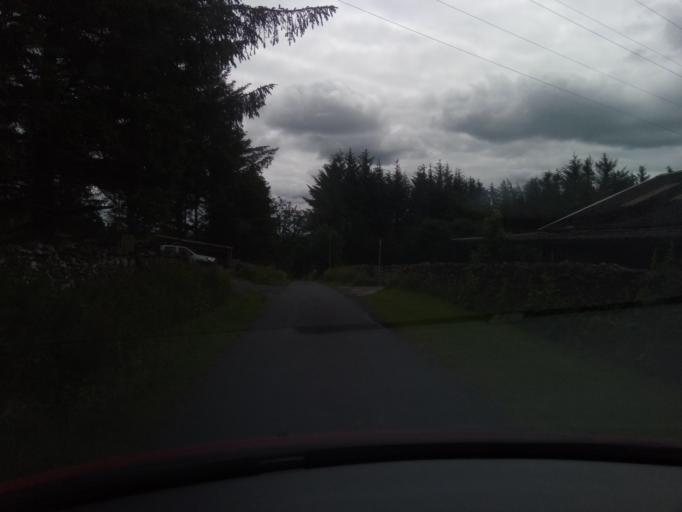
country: GB
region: Scotland
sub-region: The Scottish Borders
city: Hawick
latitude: 55.4330
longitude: -2.8232
